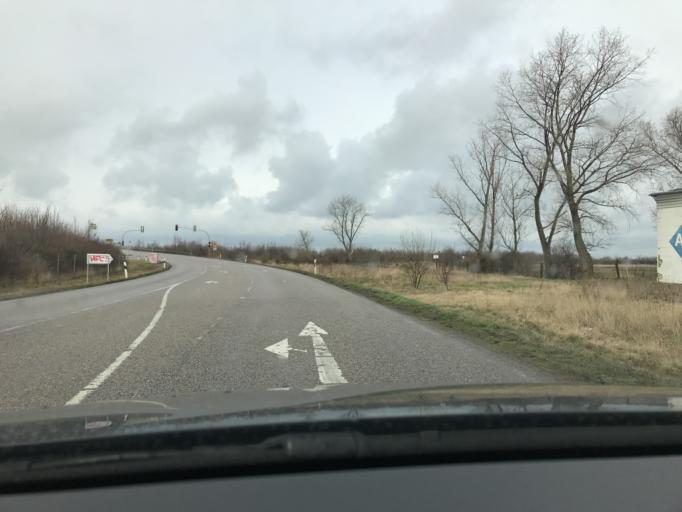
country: DE
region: Saxony-Anhalt
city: Brehna
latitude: 51.5623
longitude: 12.1982
